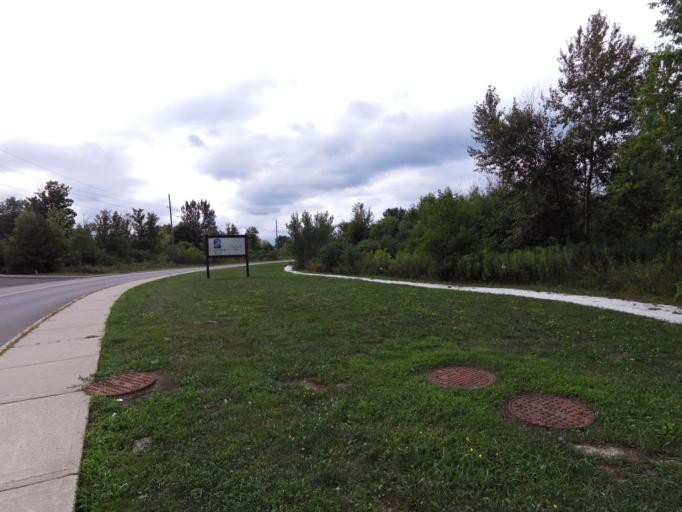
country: CA
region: Ontario
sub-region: Lanark County
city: Smiths Falls
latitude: 44.8915
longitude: -76.0267
